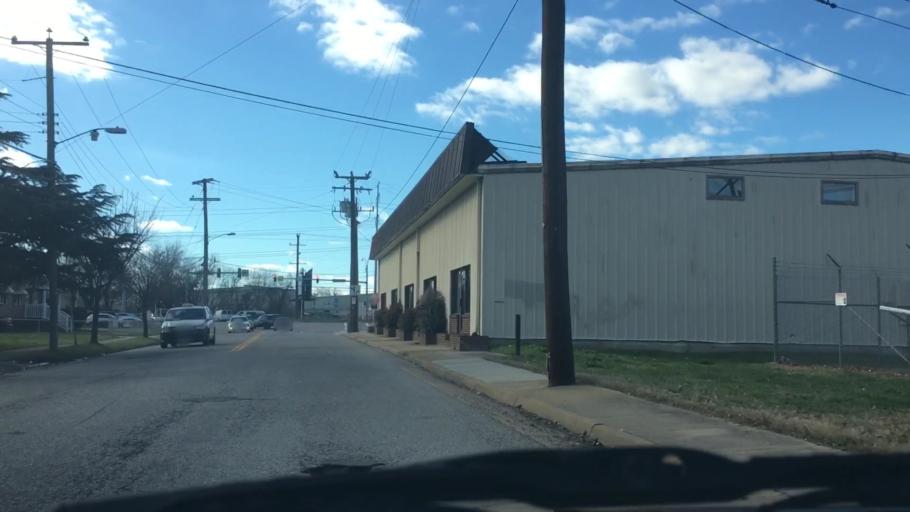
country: US
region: Virginia
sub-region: City of Norfolk
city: Norfolk
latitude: 36.9018
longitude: -76.2552
